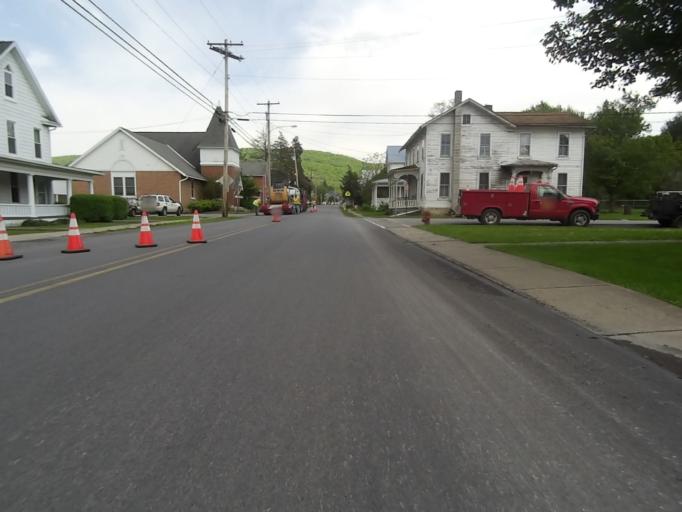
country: US
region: Pennsylvania
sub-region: Centre County
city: Zion
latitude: 41.0140
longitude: -77.6578
